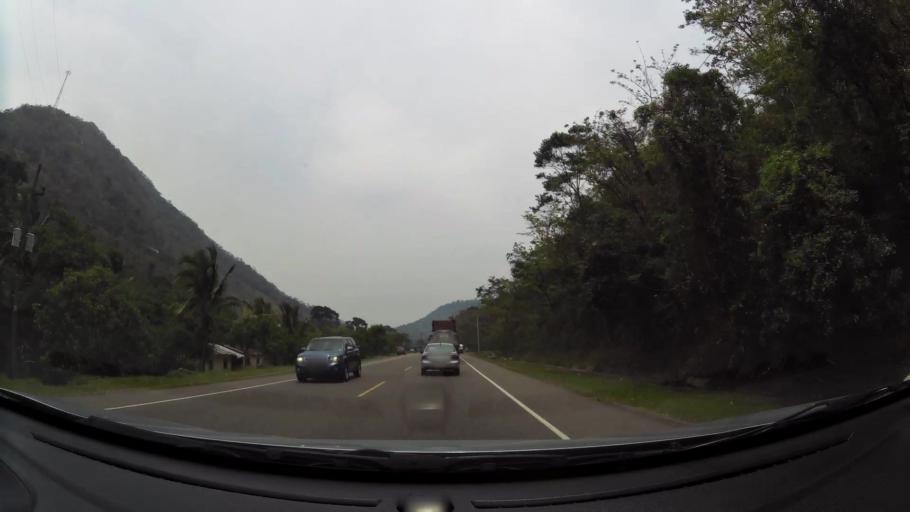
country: HN
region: Comayagua
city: Taulabe
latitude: 14.7417
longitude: -87.9631
